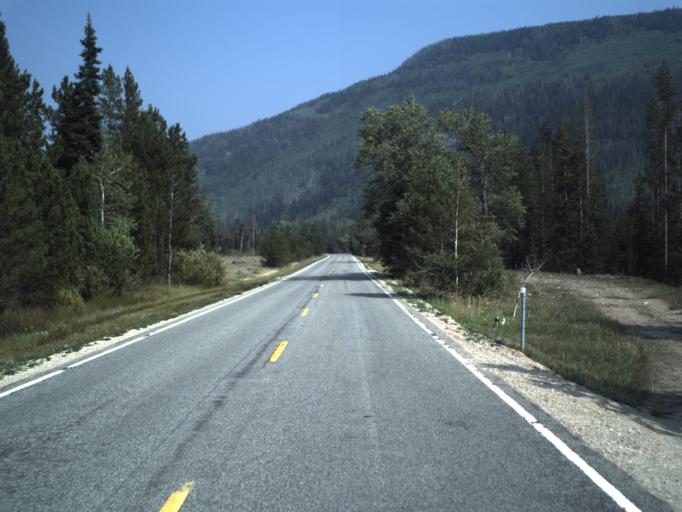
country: US
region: Utah
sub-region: Summit County
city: Francis
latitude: 40.5779
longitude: -111.0365
